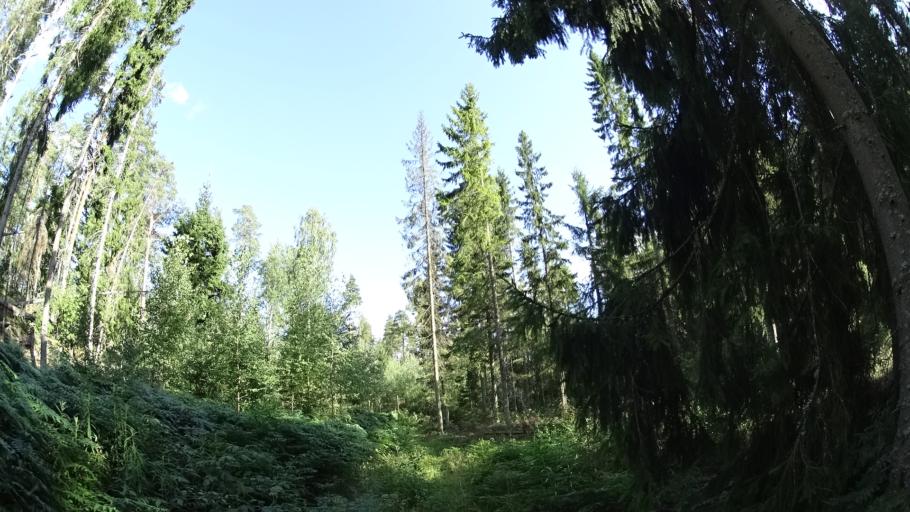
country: FI
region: Uusimaa
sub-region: Helsinki
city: Vihti
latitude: 60.3734
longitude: 24.3757
